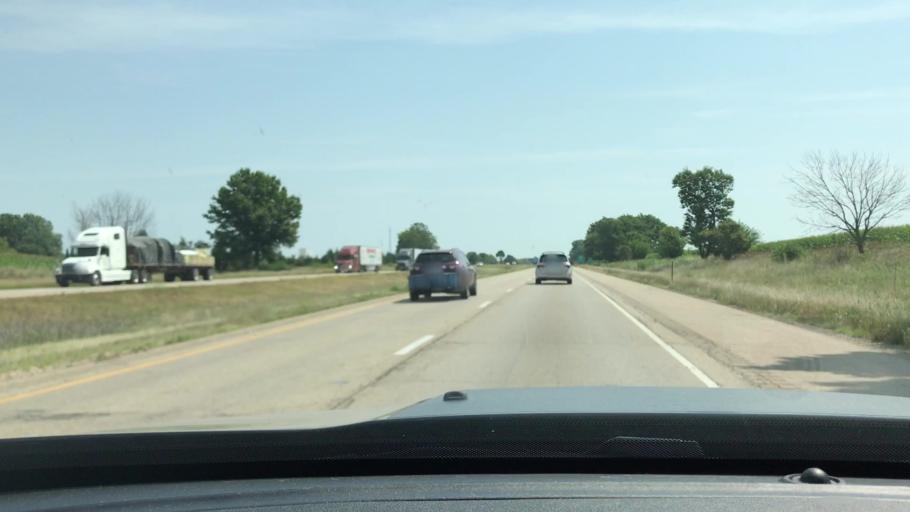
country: US
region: Illinois
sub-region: Bureau County
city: Princeton
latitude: 41.3969
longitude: -89.4875
